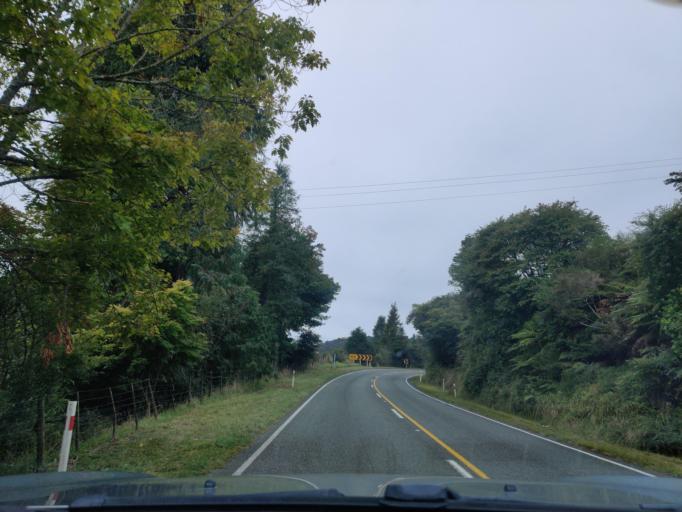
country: NZ
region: West Coast
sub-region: Buller District
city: Westport
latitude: -41.8416
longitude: 171.9058
